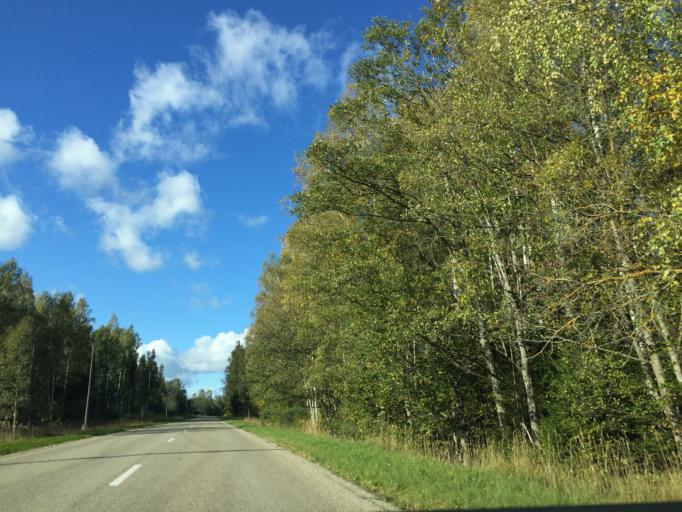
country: LV
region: Rojas
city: Roja
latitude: 57.4239
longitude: 22.9216
